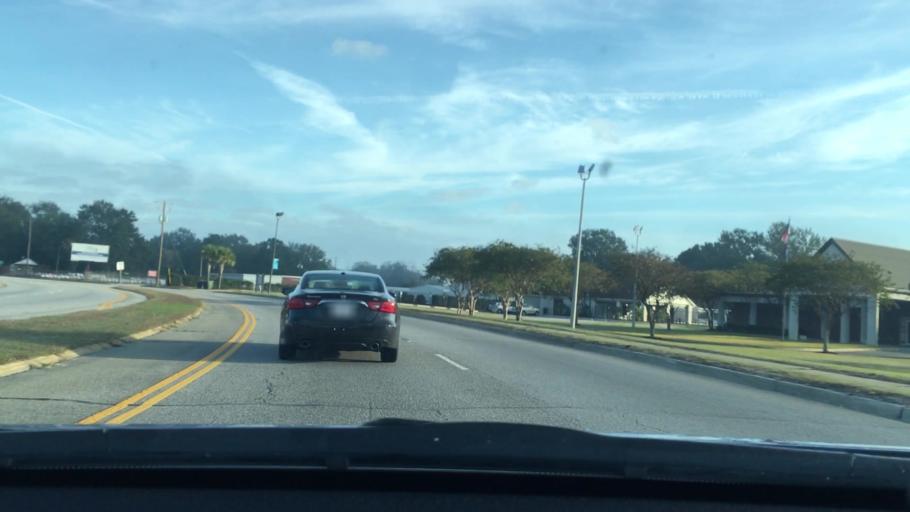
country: US
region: South Carolina
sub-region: Sumter County
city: South Sumter
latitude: 33.8972
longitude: -80.3369
